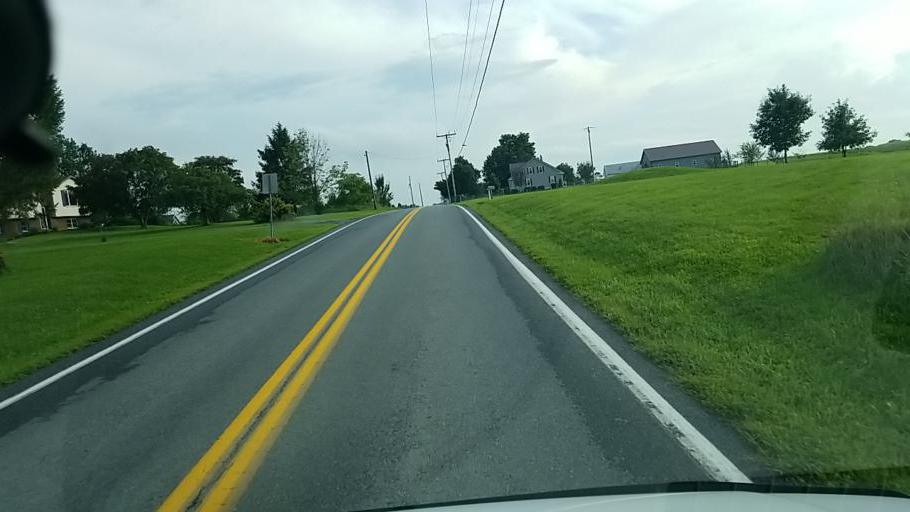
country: US
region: Pennsylvania
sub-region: Cumberland County
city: Newville
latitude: 40.2323
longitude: -77.4528
